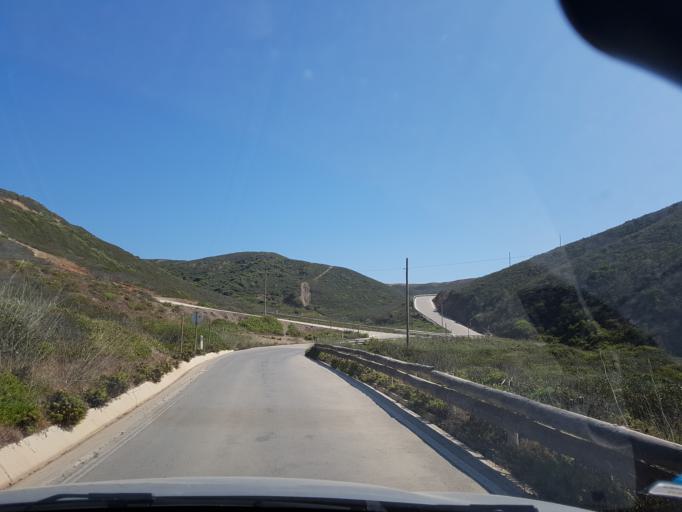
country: PT
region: Faro
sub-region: Vila do Bispo
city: Vila do Bispo
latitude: 37.1055
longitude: -8.9335
